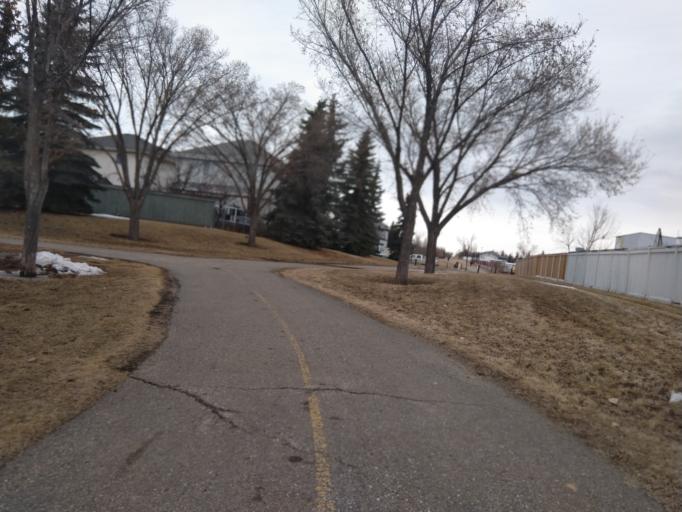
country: CA
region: Alberta
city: Calgary
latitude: 51.1563
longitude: -114.0480
